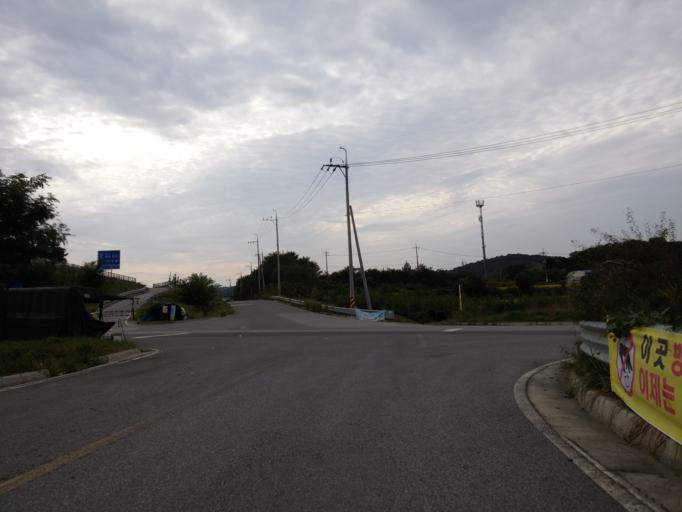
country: KR
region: Chungcheongnam-do
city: Yonmu
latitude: 36.1646
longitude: 127.1879
